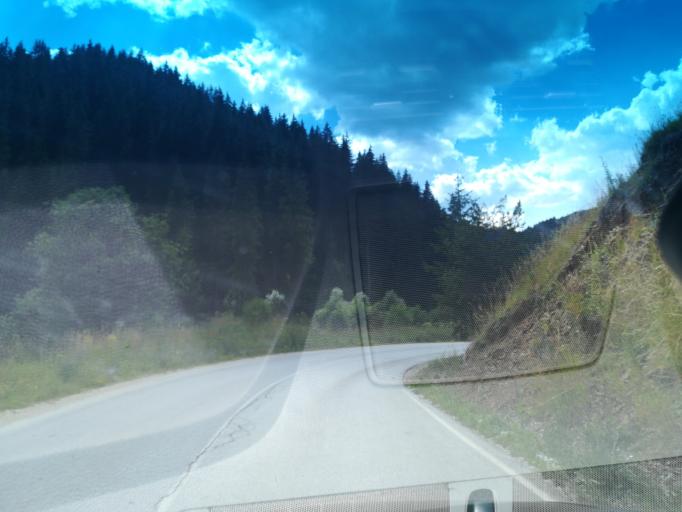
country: BG
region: Smolyan
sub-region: Obshtina Chepelare
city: Chepelare
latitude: 41.6622
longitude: 24.6424
